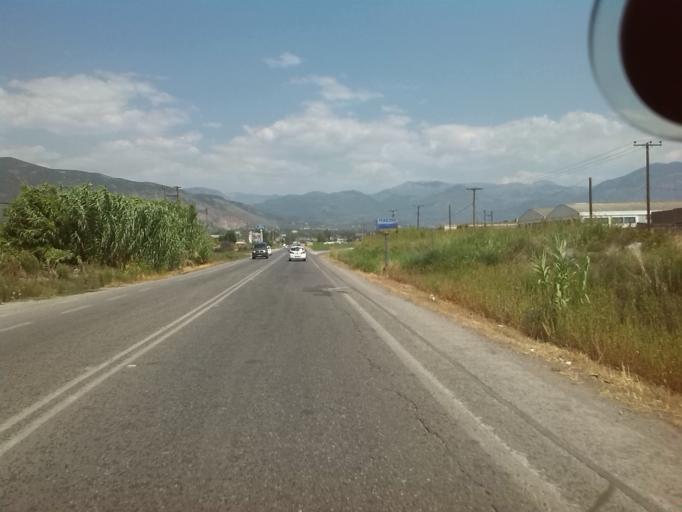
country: GR
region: Peloponnese
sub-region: Nomos Messinias
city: Sperkhoyia
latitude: 37.0562
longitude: 22.0500
